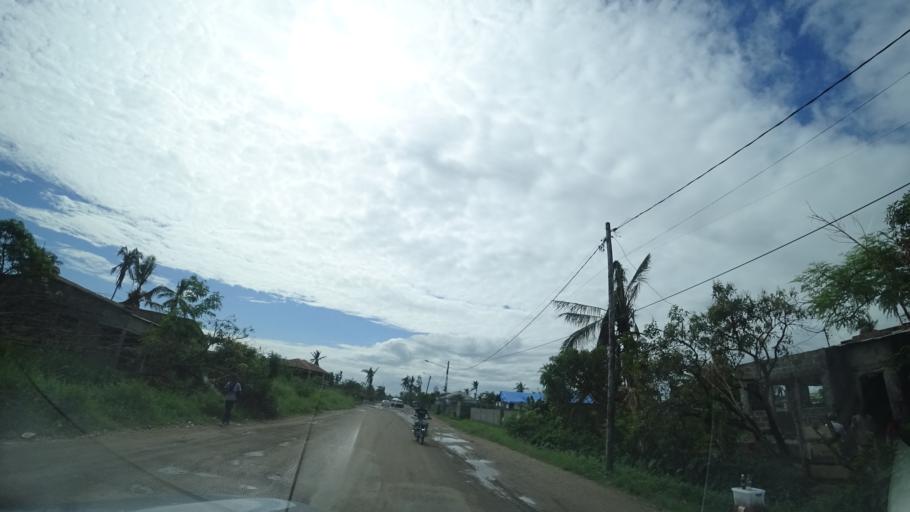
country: MZ
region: Sofala
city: Beira
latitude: -19.7645
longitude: 34.8667
